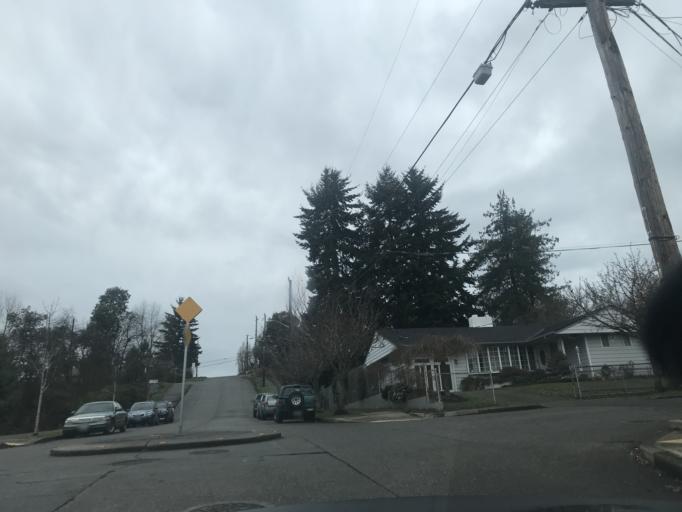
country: US
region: Washington
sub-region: King County
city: White Center
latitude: 47.5319
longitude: -122.3656
